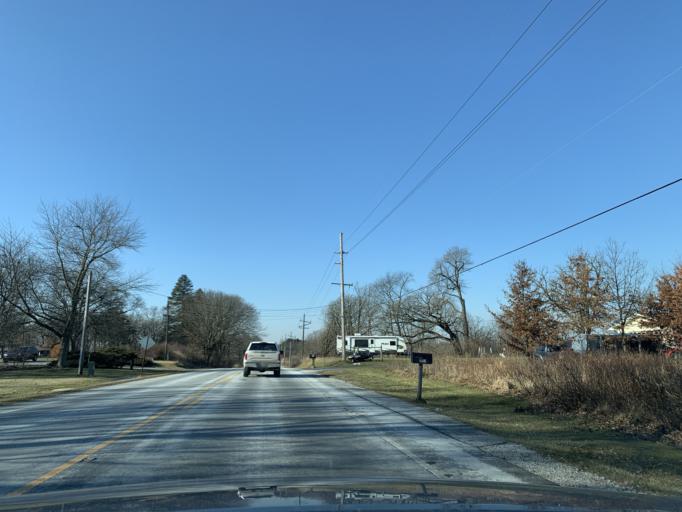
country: US
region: Indiana
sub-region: Lake County
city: Crown Point
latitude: 41.4207
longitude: -87.4087
